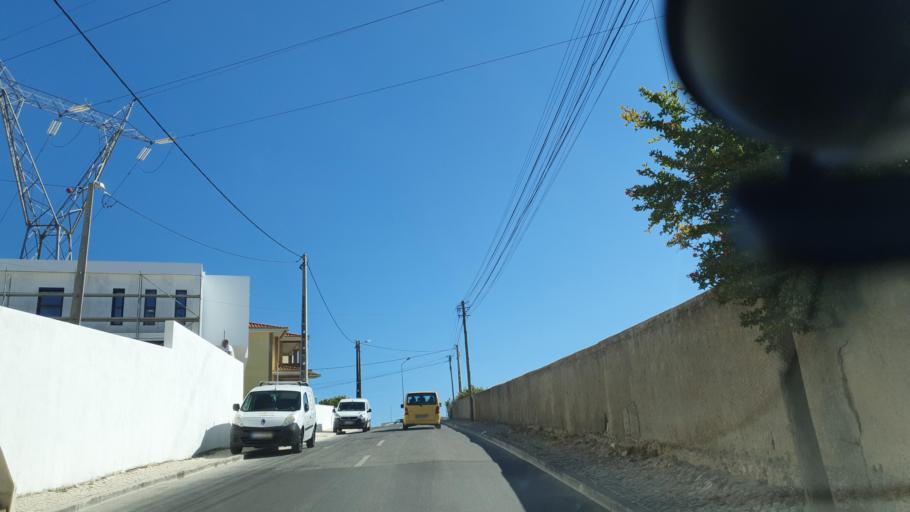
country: PT
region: Lisbon
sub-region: Sintra
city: Belas
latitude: 38.8008
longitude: -9.2512
